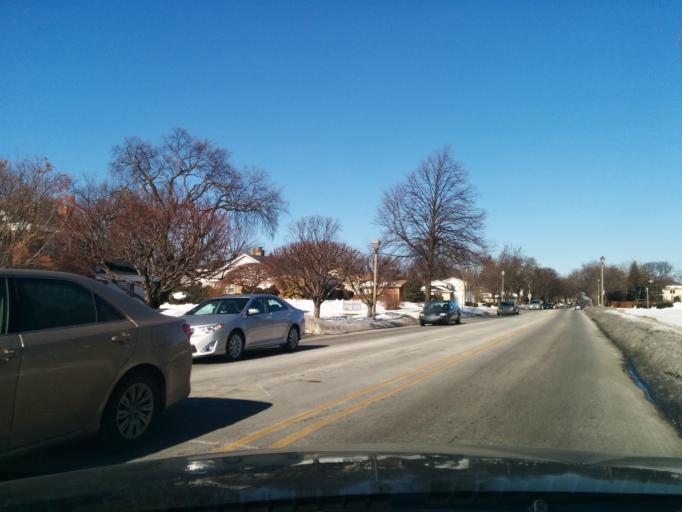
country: US
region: Illinois
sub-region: DuPage County
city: Elmhurst
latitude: 41.8904
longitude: -87.9399
